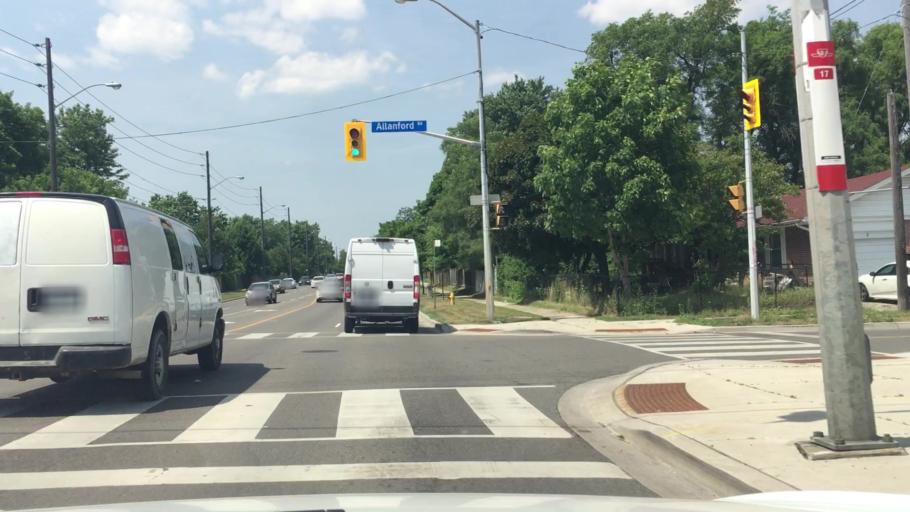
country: CA
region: Ontario
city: Scarborough
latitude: 43.7742
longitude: -79.2950
